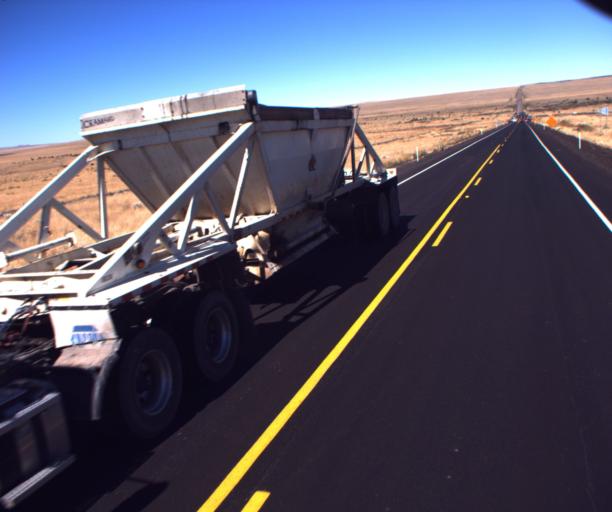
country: US
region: Arizona
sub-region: Apache County
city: Springerville
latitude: 34.2756
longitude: -109.3641
